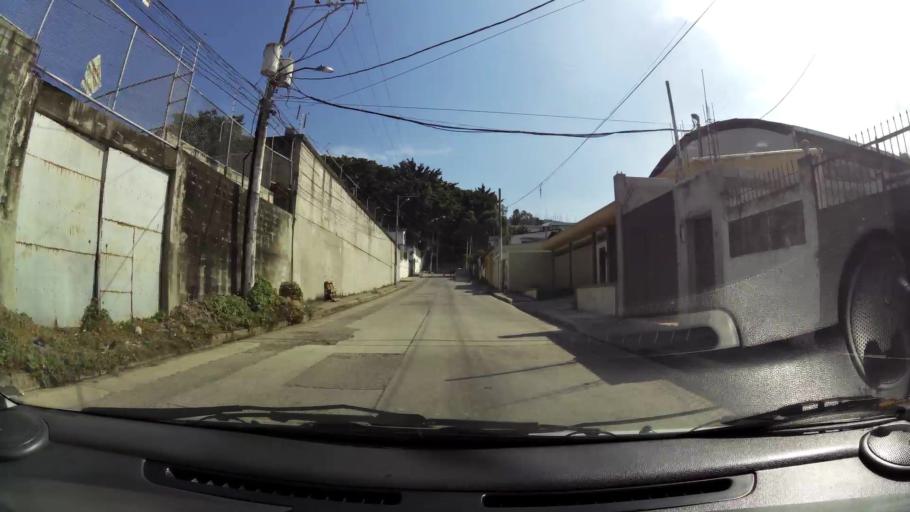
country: EC
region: Guayas
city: Guayaquil
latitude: -2.1625
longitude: -79.9363
